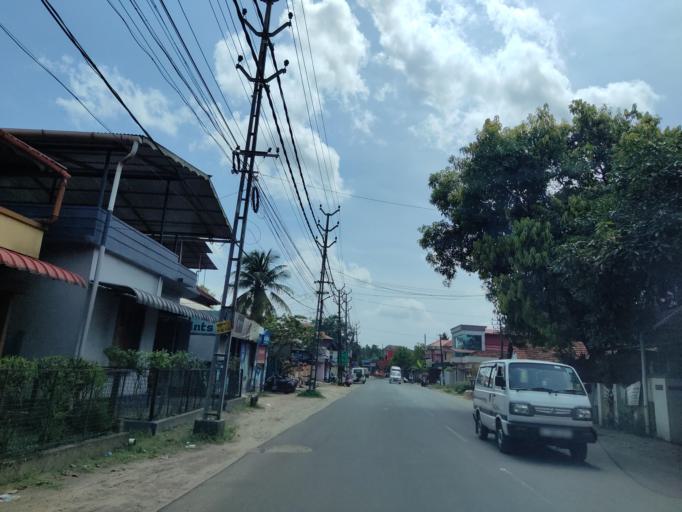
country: IN
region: Kerala
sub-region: Alappuzha
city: Mavelikara
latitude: 9.2547
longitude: 76.5500
